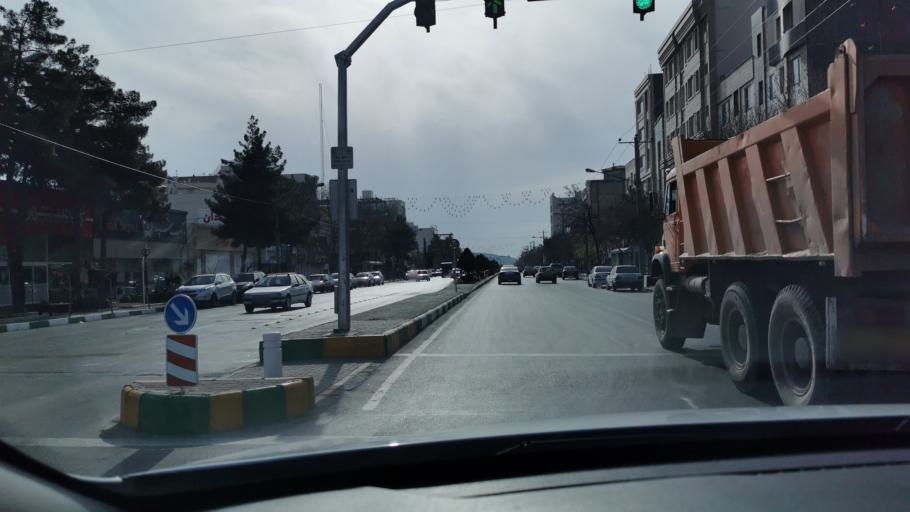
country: IR
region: Razavi Khorasan
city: Mashhad
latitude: 36.2910
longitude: 59.5379
